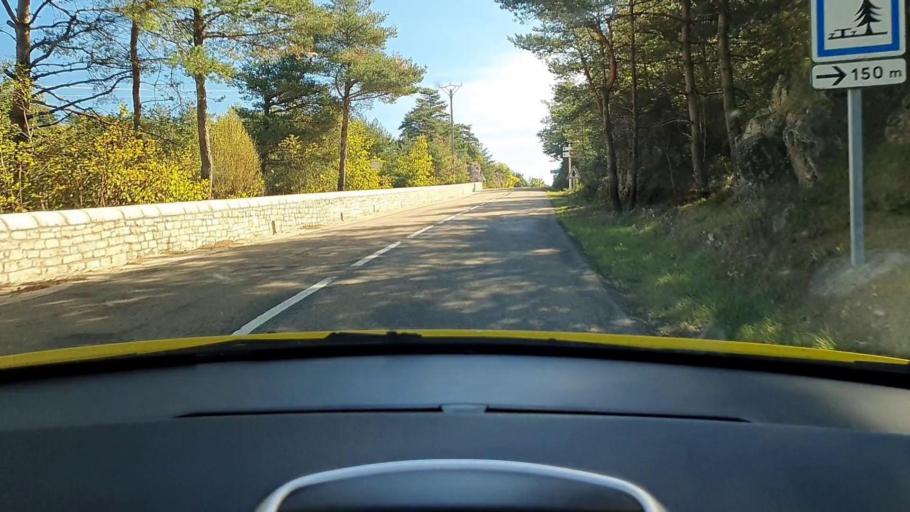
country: FR
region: Languedoc-Roussillon
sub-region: Departement du Gard
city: Le Vigan
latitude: 43.9678
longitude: 3.3990
